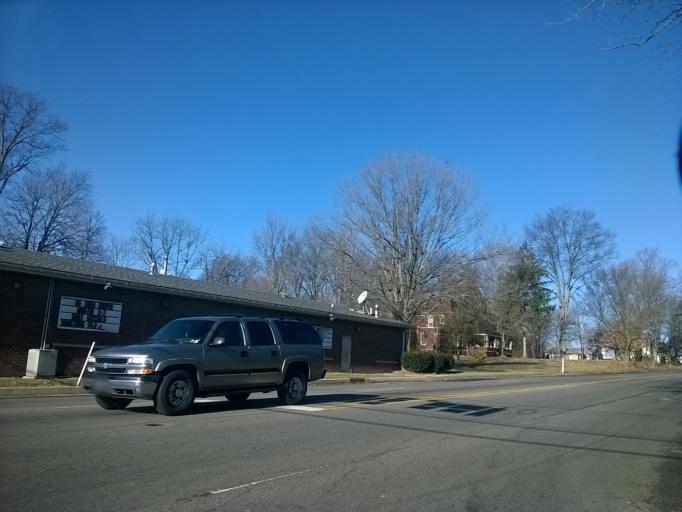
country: US
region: Indiana
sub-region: Scott County
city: Austin
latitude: 38.7424
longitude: -85.8046
